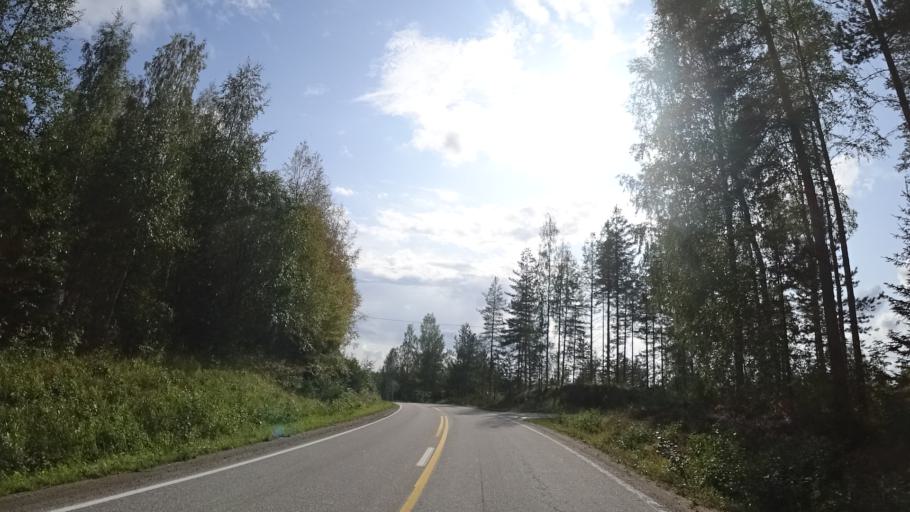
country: FI
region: North Karelia
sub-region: Pielisen Karjala
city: Lieksa
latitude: 63.4019
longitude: 30.0807
